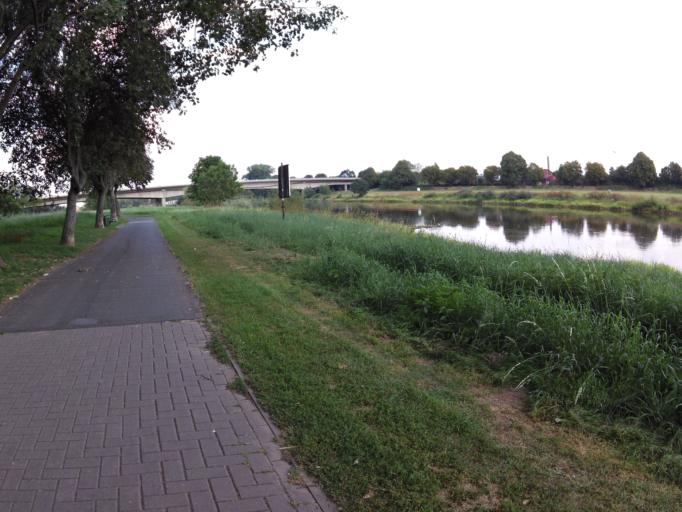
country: DE
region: North Rhine-Westphalia
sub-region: Regierungsbezirk Detmold
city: Minden
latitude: 52.2956
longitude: 8.9276
